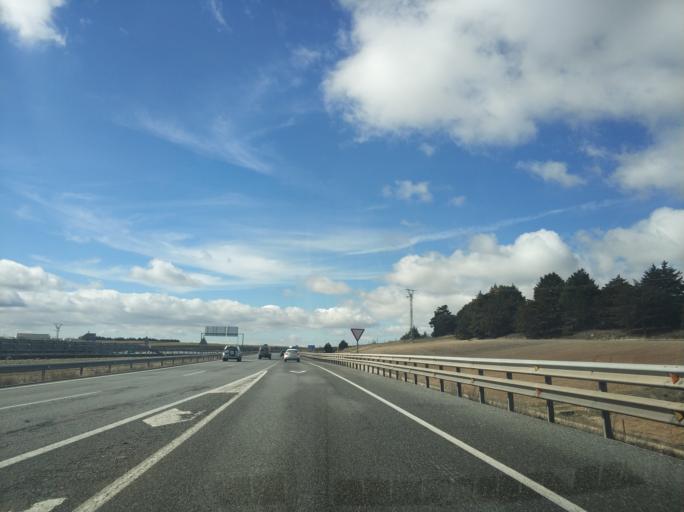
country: ES
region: Castille and Leon
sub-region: Provincia de Burgos
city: Villagonzalo-Pedernales
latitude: 42.3153
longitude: -3.7054
